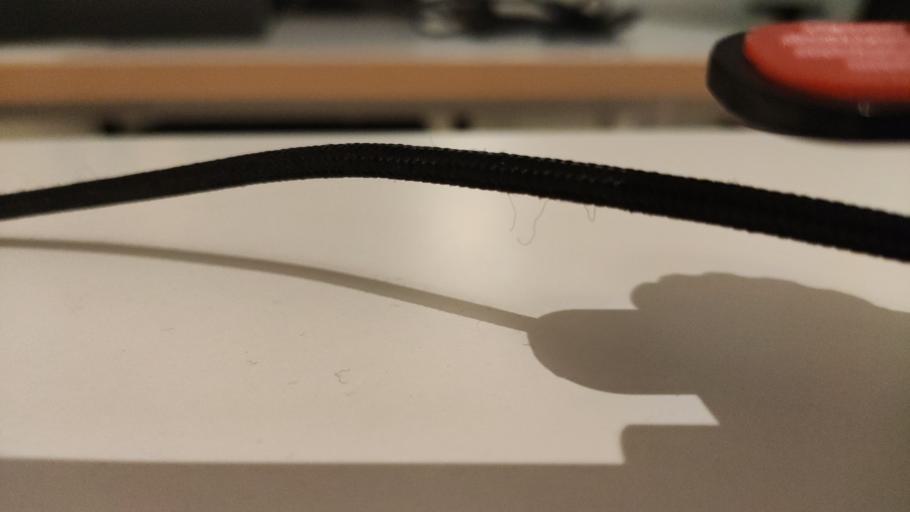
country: RU
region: Moskovskaya
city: Novoye
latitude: 55.6252
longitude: 38.9461
